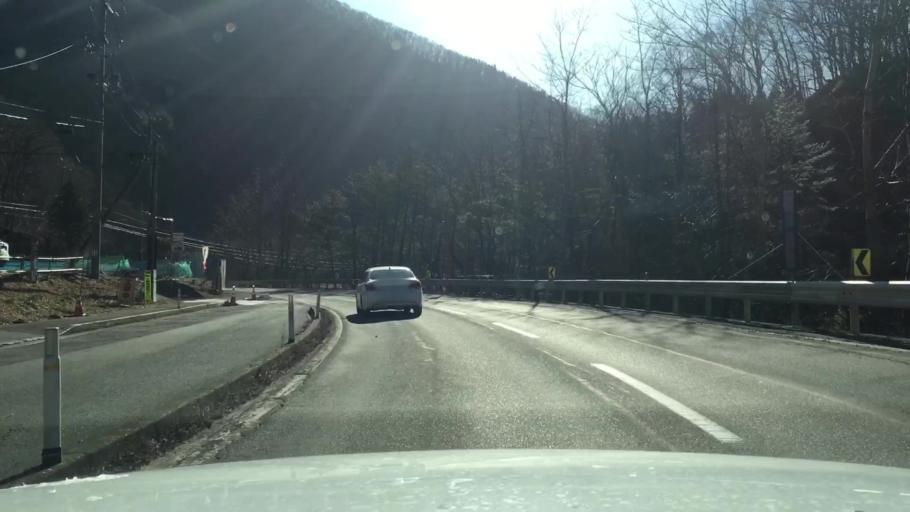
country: JP
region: Iwate
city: Miyako
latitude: 39.6090
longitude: 141.6497
